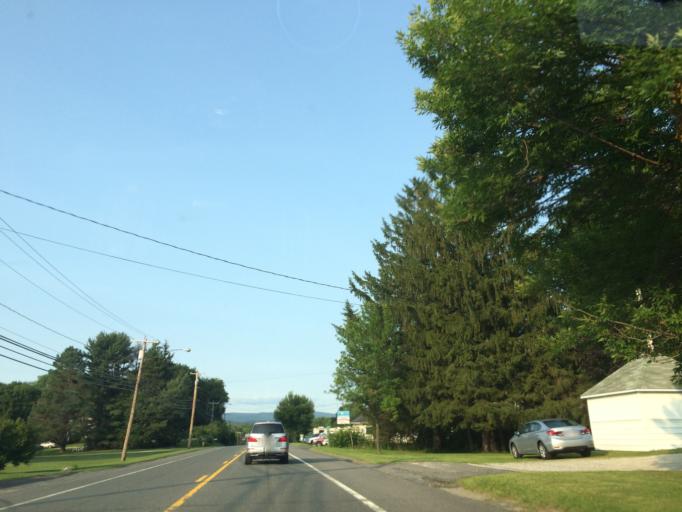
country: US
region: Massachusetts
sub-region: Berkshire County
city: Pittsfield
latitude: 42.4338
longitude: -73.3117
